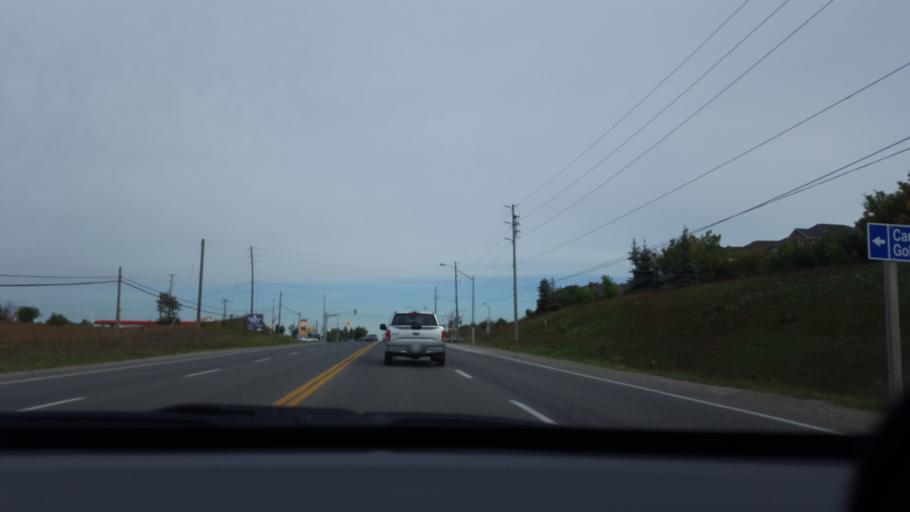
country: CA
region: Ontario
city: Vaughan
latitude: 43.8903
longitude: -79.5206
